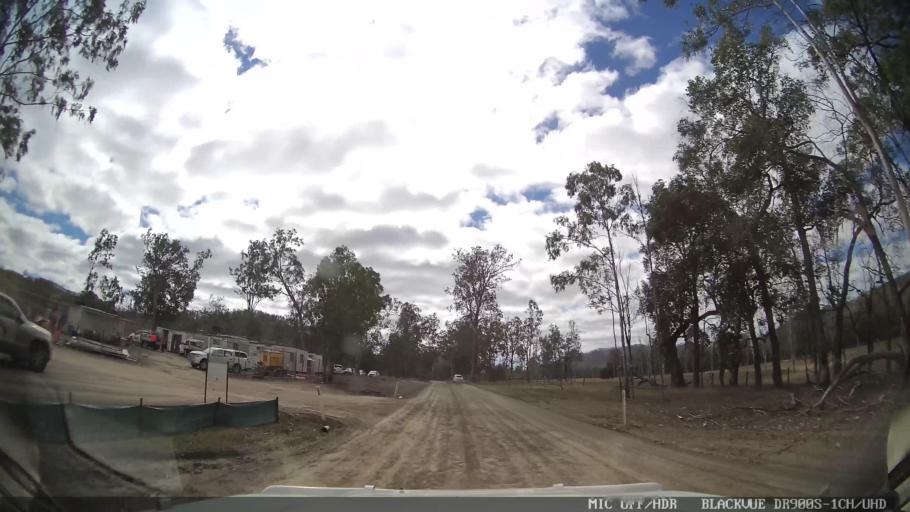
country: AU
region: Queensland
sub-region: Gladstone
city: Toolooa
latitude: -24.6129
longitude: 151.3003
